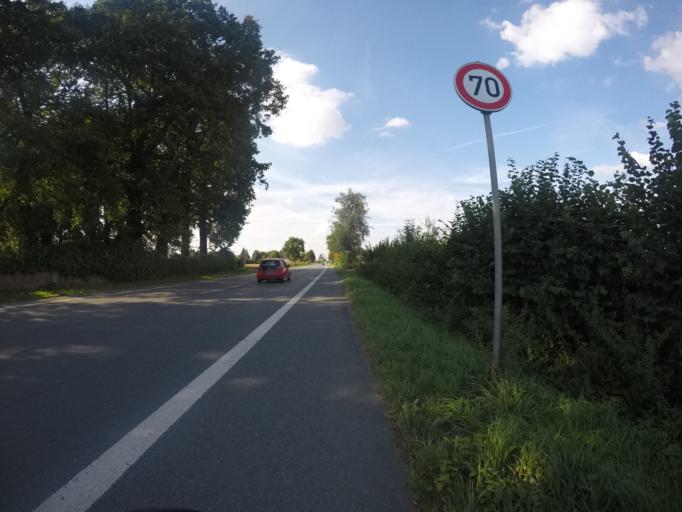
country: DE
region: North Rhine-Westphalia
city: Enger
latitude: 52.0882
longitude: 8.5860
